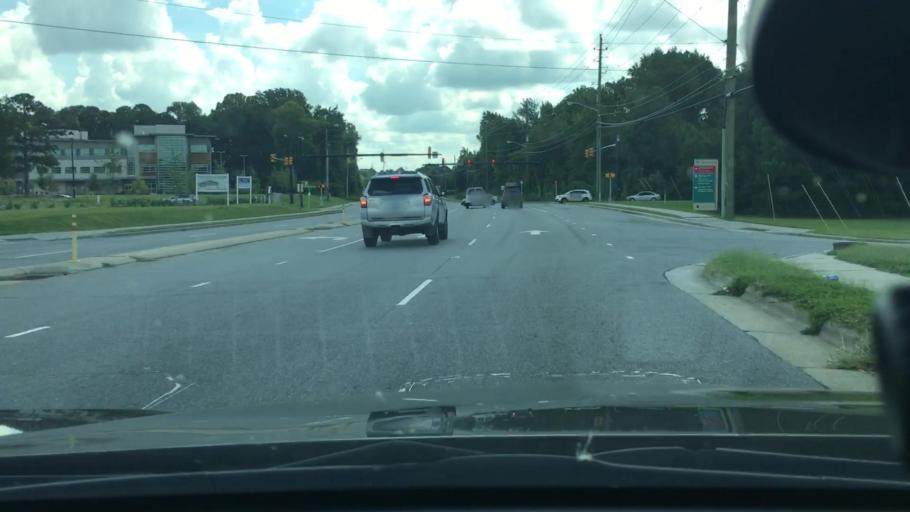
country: US
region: North Carolina
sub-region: Pitt County
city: Greenville
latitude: 35.6164
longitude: -77.4101
